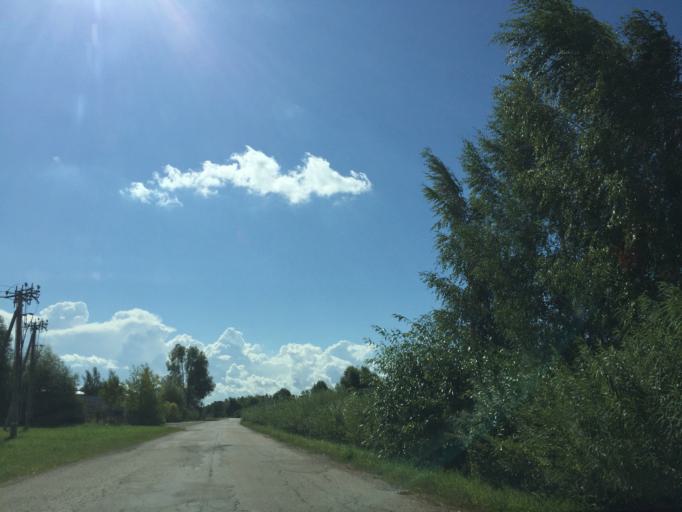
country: LV
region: Bauskas Rajons
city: Bauska
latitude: 56.4170
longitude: 24.1776
